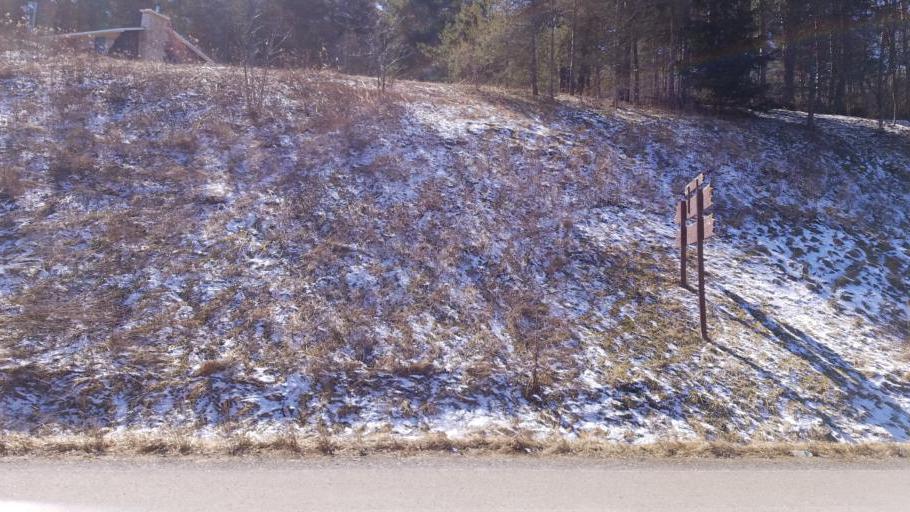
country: US
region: New York
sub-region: Allegany County
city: Wellsville
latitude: 41.9968
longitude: -77.8785
